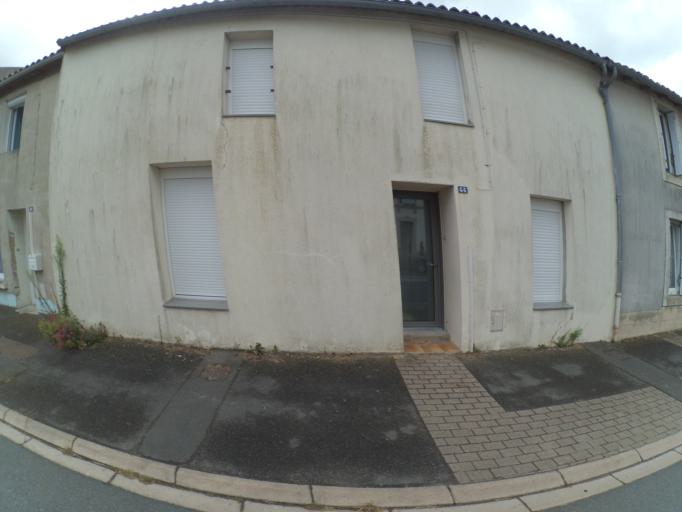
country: FR
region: Pays de la Loire
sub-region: Departement de Maine-et-Loire
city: Montfaucon-Montigne
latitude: 47.0871
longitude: -1.1353
